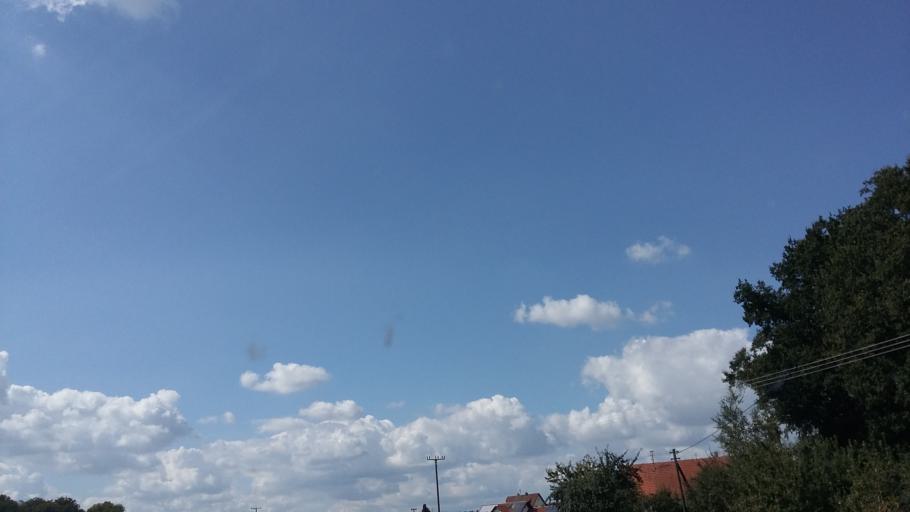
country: DE
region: Bavaria
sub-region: Swabia
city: Holzheim
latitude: 48.3518
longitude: 10.1181
